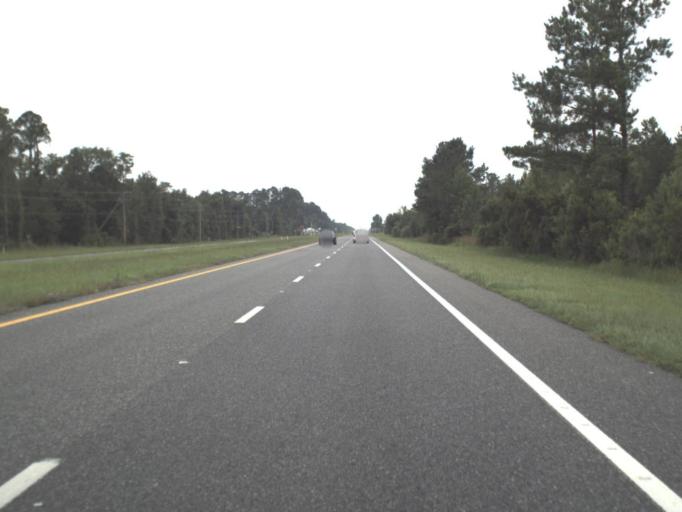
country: US
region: Florida
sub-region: Levy County
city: Bronson
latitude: 29.3211
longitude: -82.7645
